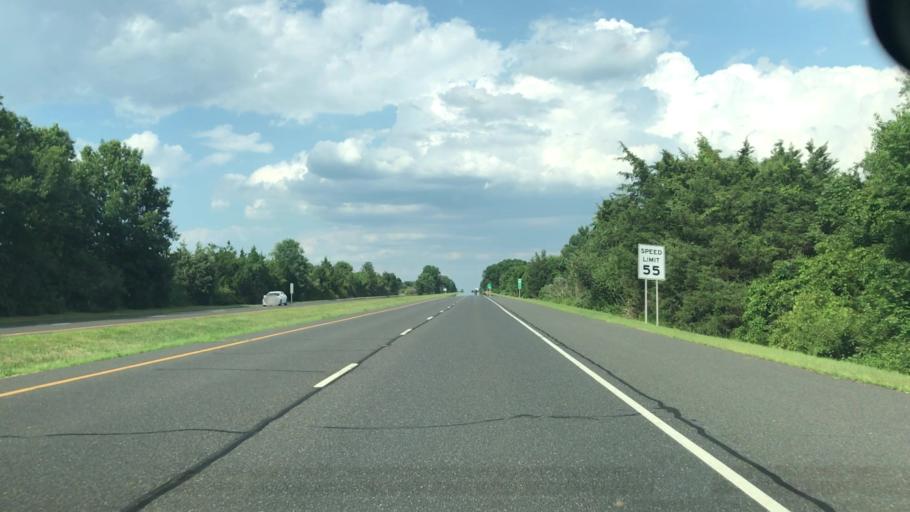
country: US
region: New Jersey
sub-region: Hunterdon County
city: Lambertville
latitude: 40.4081
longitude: -74.9030
